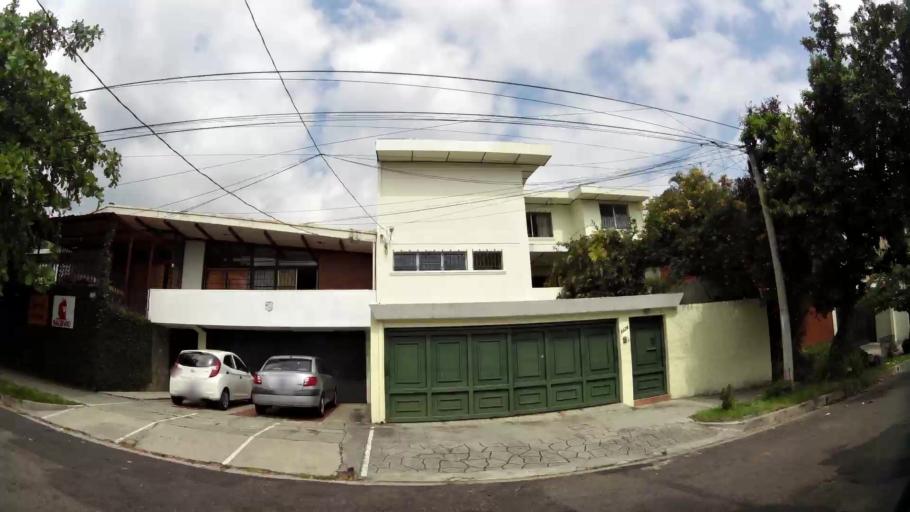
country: SV
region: La Libertad
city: Santa Tecla
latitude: 13.7054
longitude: -89.2511
